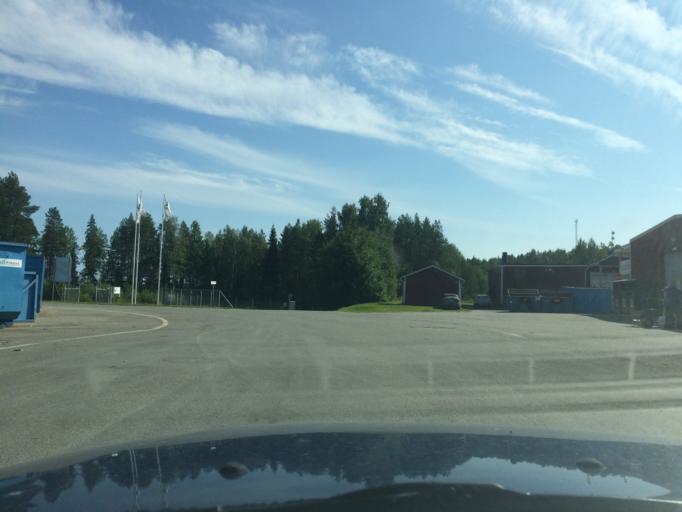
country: SE
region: Norrbotten
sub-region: Pitea Kommun
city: Norrfjarden
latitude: 65.3760
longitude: 21.3897
